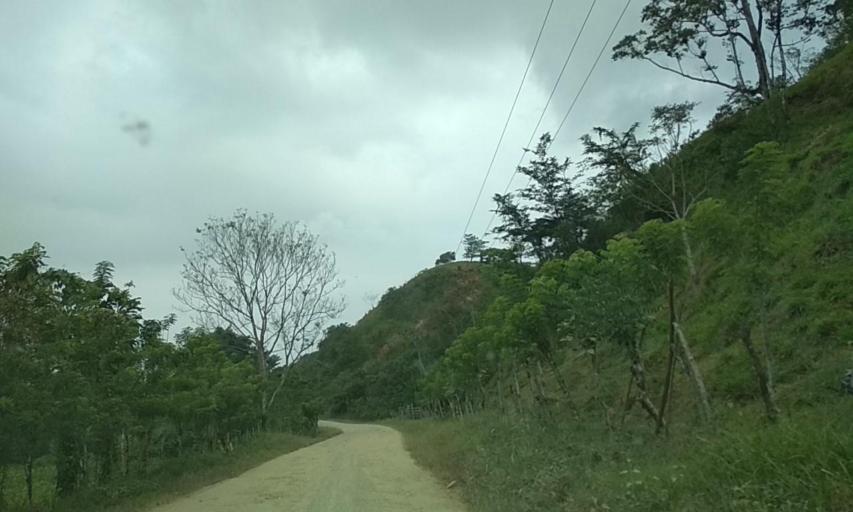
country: MX
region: Veracruz
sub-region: Uxpanapa
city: Poblado 10
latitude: 17.4526
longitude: -94.0875
